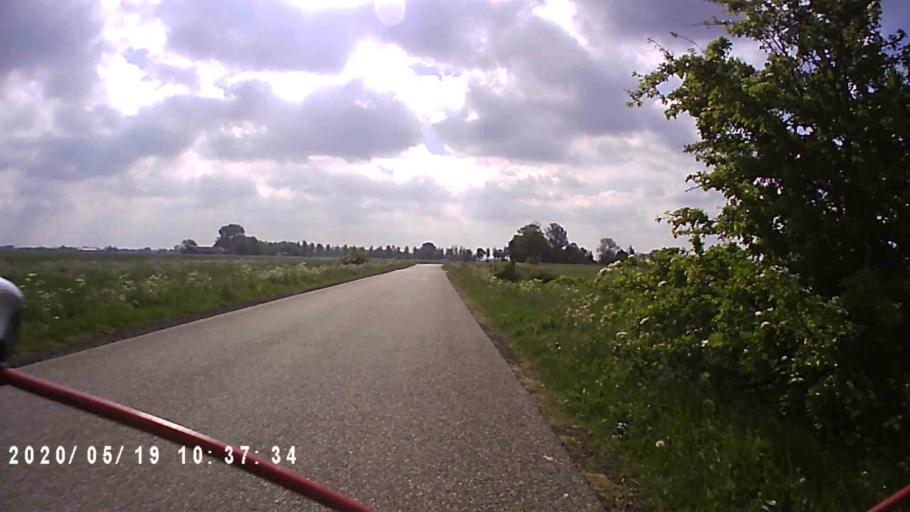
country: NL
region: Friesland
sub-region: Gemeente Kollumerland en Nieuwkruisland
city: Kollum
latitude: 53.2746
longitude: 6.1847
